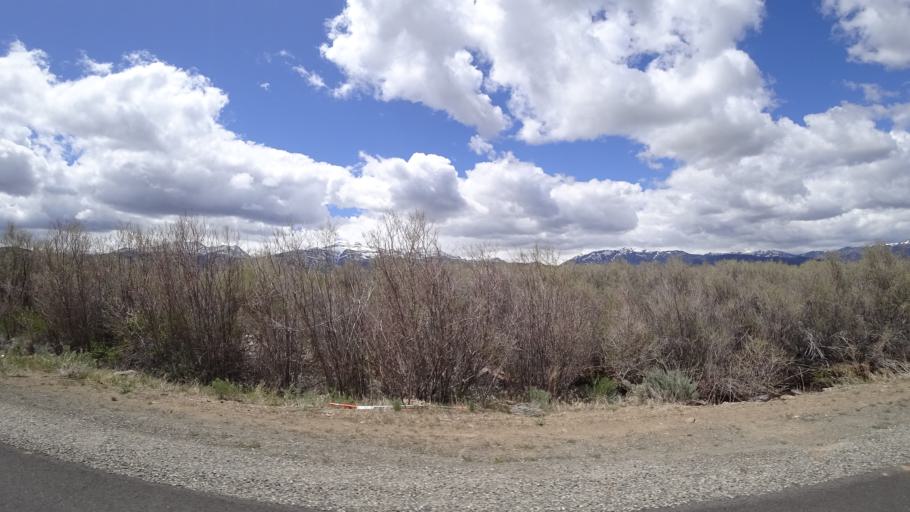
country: US
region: California
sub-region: Mono County
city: Bridgeport
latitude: 38.1985
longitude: -119.2207
